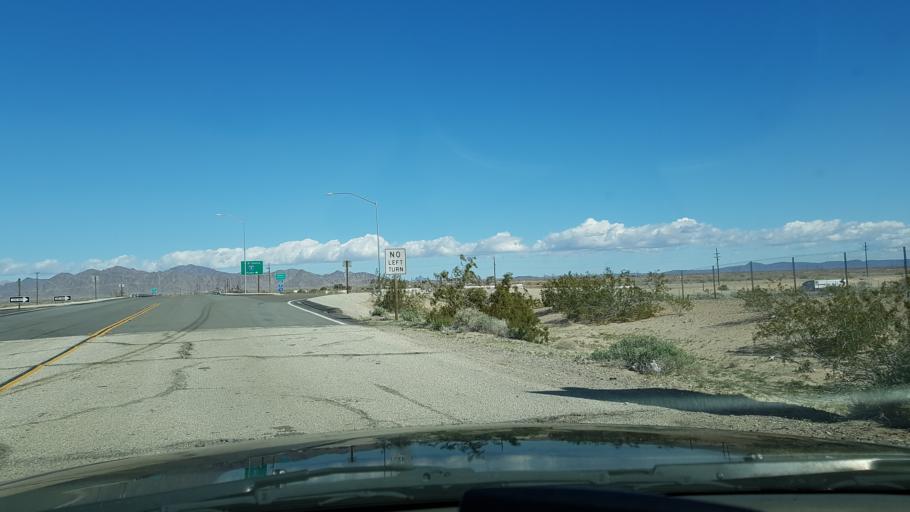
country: MX
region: Baja California
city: Los Algodones
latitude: 32.7452
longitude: -114.7547
